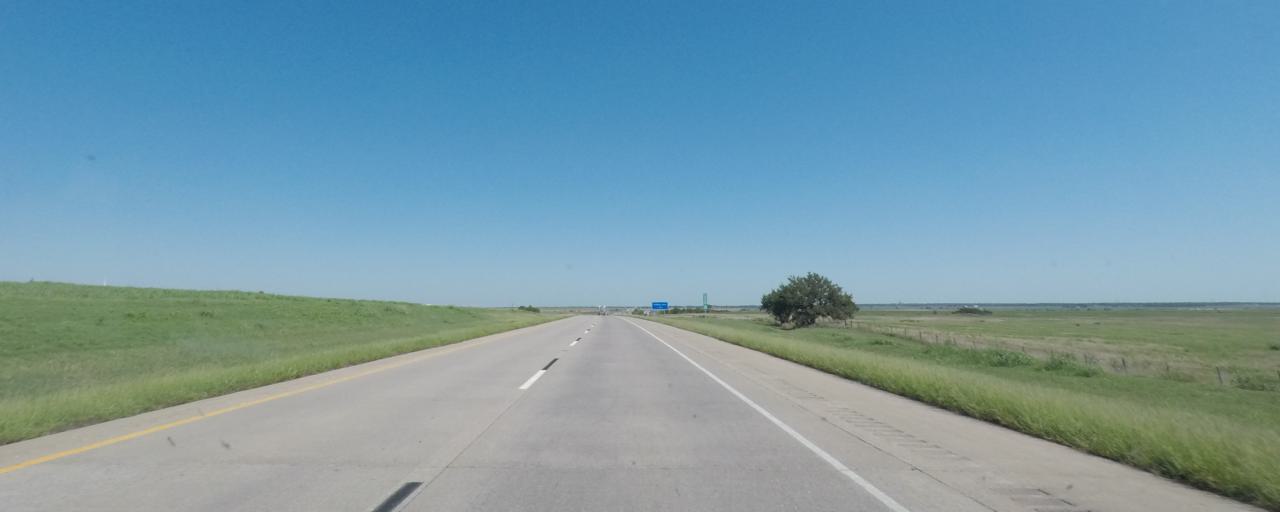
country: US
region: Oklahoma
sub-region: Kay County
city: Tonkawa
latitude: 36.5950
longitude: -97.3454
